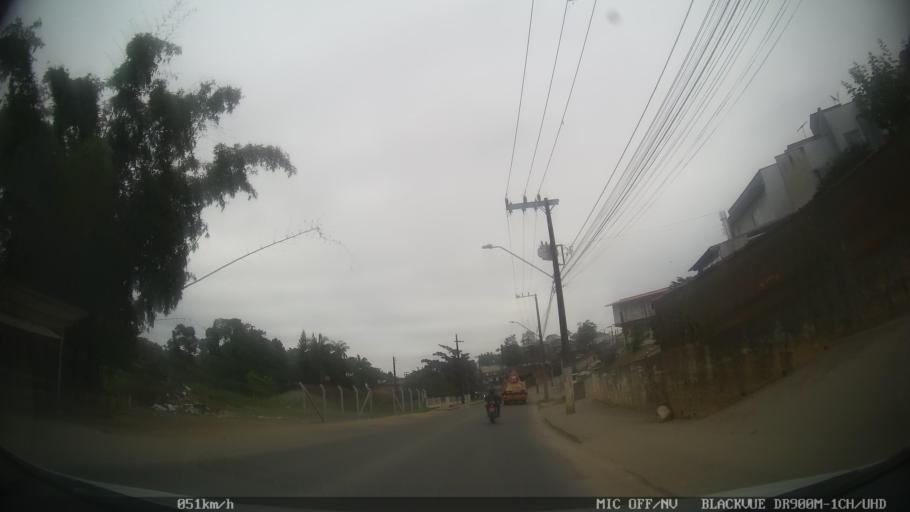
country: BR
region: Santa Catarina
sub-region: Joinville
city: Joinville
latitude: -26.3362
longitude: -48.8057
